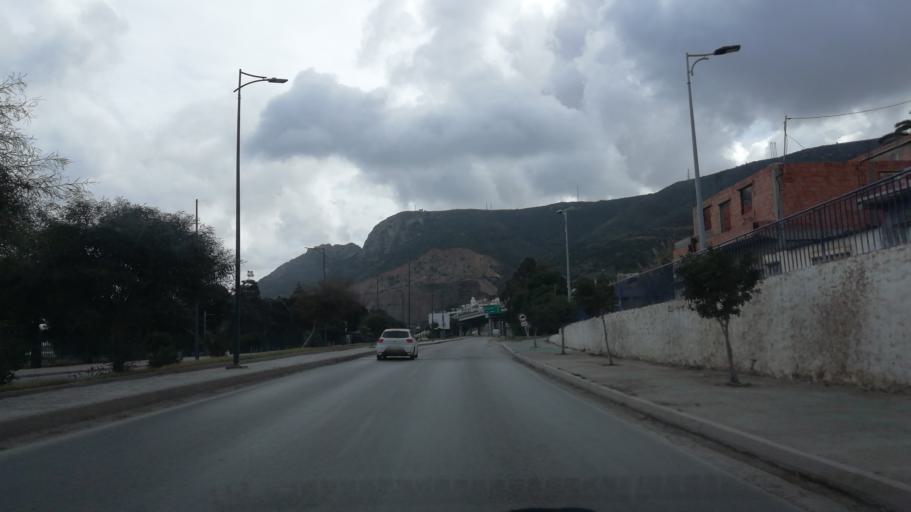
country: DZ
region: Oran
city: Mers el Kebir
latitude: 35.7164
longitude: -0.6945
